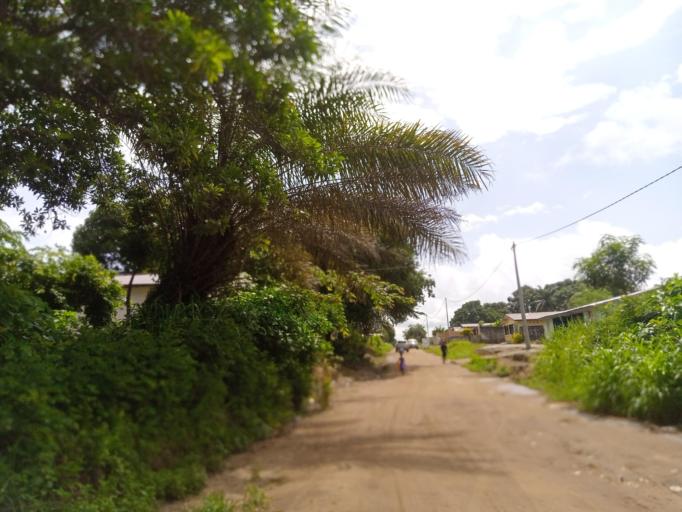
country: SL
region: Northern Province
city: Tintafor
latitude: 8.6259
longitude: -13.2103
